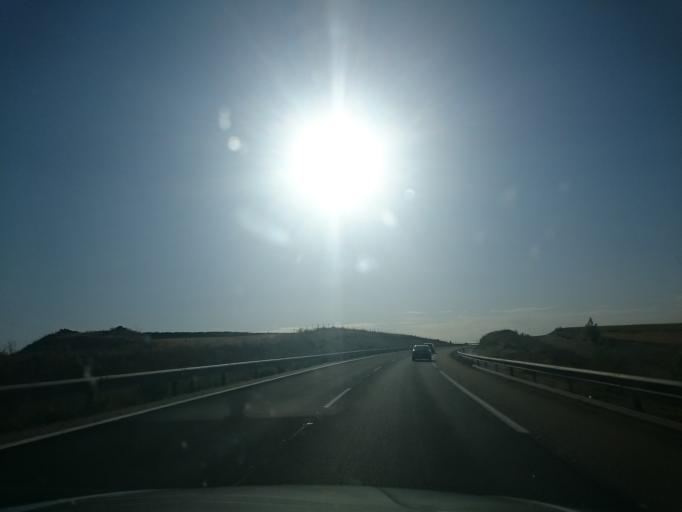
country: ES
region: Castille and Leon
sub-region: Provincia de Burgos
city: Villagonzalo-Pedernales
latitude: 42.3047
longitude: -3.7494
